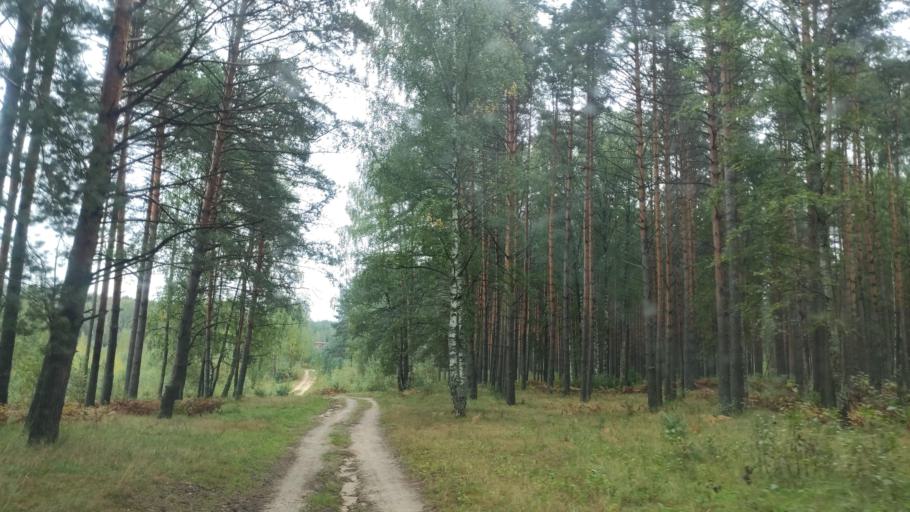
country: RU
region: Nizjnij Novgorod
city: Taremskoye
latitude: 55.9976
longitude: 42.9831
